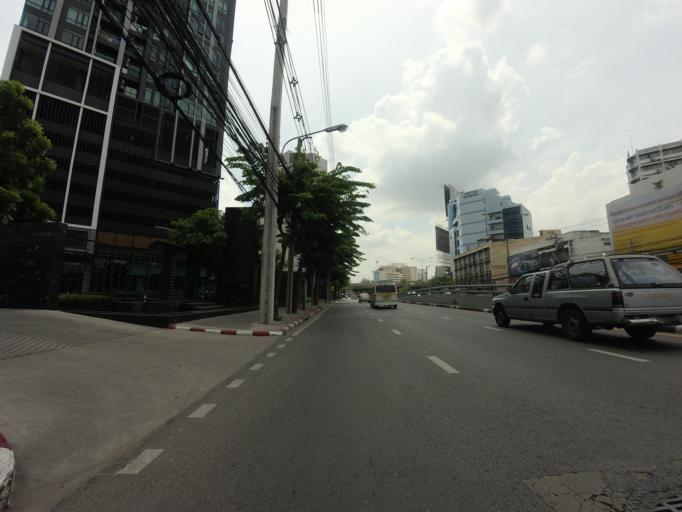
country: TH
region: Bangkok
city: Din Daeng
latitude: 13.7637
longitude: 100.5458
